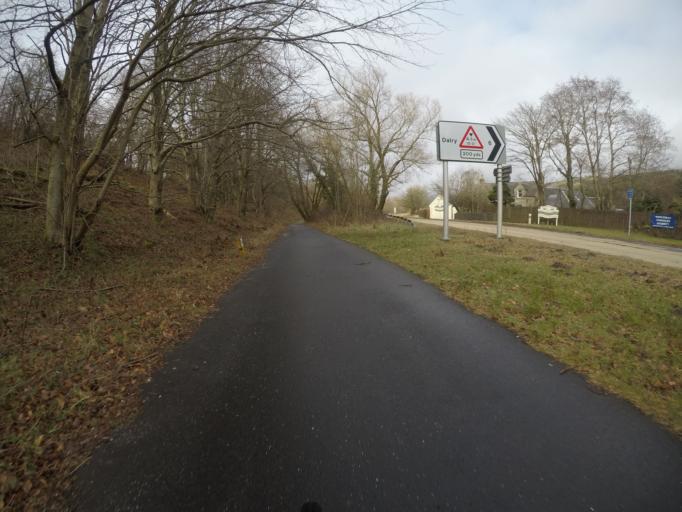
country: GB
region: Scotland
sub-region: North Ayrshire
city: Fairlie
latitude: 55.7370
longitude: -4.8615
